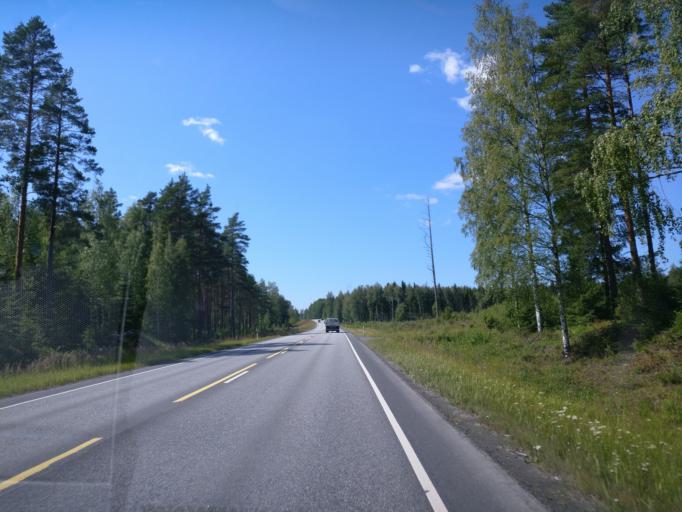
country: FI
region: Satakunta
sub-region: Pori
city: Kullaa
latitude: 61.4612
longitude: 22.1214
